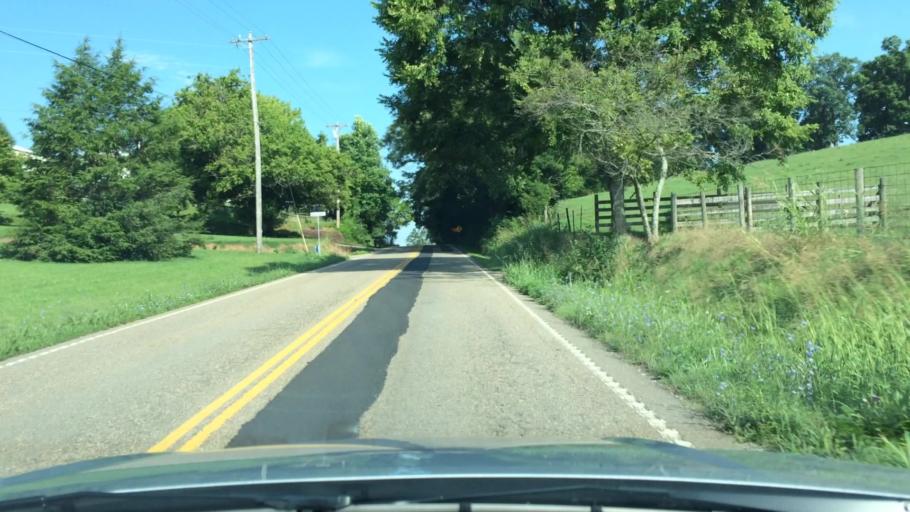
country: US
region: Tennessee
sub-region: Jefferson County
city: White Pine
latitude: 36.1500
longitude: -83.3454
